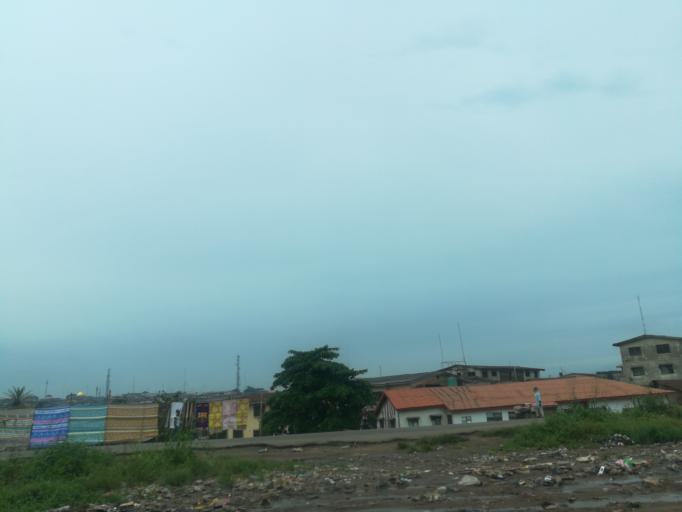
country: NG
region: Oyo
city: Ibadan
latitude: 7.3995
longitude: 3.9415
